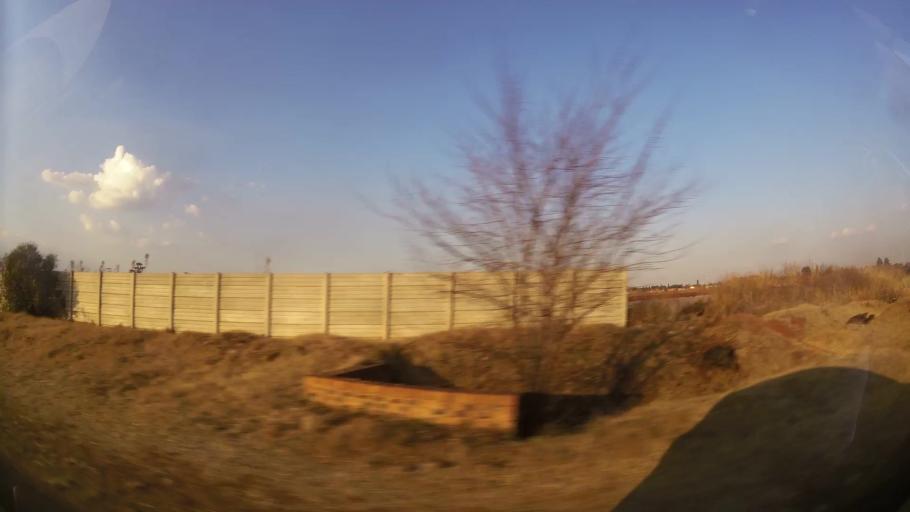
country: ZA
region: Gauteng
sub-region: Ekurhuleni Metropolitan Municipality
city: Germiston
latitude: -26.2995
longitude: 28.2316
